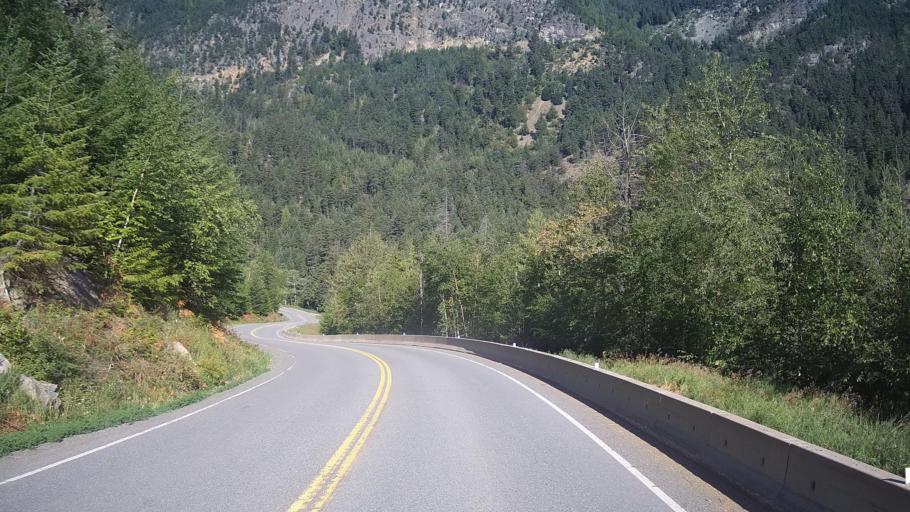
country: CA
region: British Columbia
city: Lillooet
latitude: 50.6385
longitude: -122.0830
